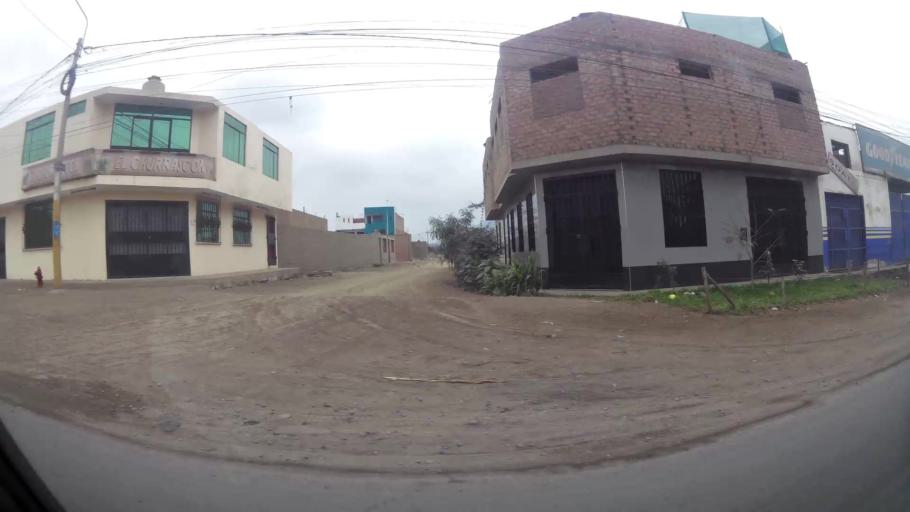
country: PE
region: Lima
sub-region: Provincia de Huaral
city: Huaral
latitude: -11.5004
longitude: -77.2219
